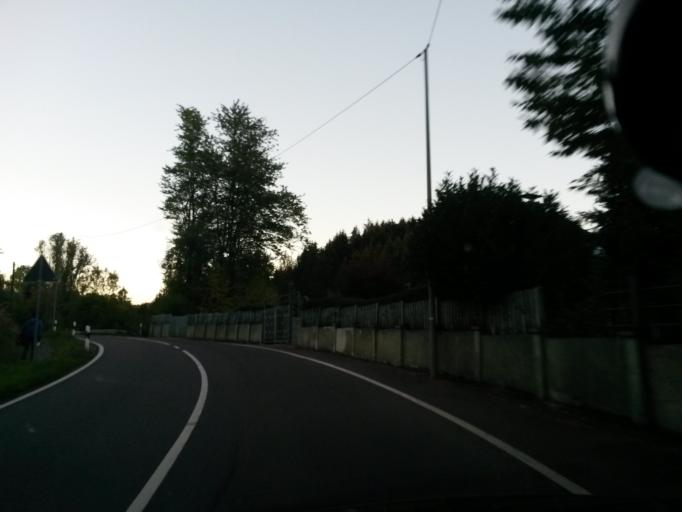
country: DE
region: North Rhine-Westphalia
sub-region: Regierungsbezirk Koln
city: Engelskirchen
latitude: 51.0069
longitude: 7.4696
